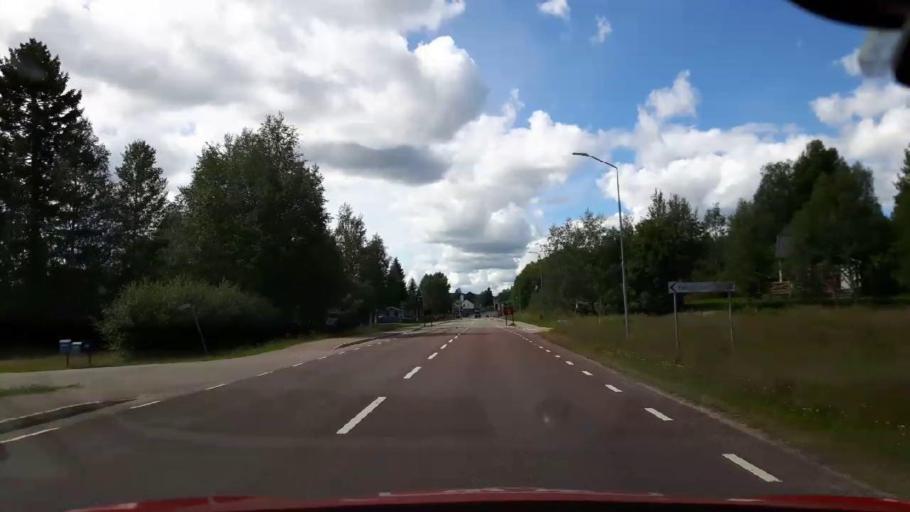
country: SE
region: Jaemtland
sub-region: Harjedalens Kommun
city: Sveg
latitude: 61.8531
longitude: 14.0817
